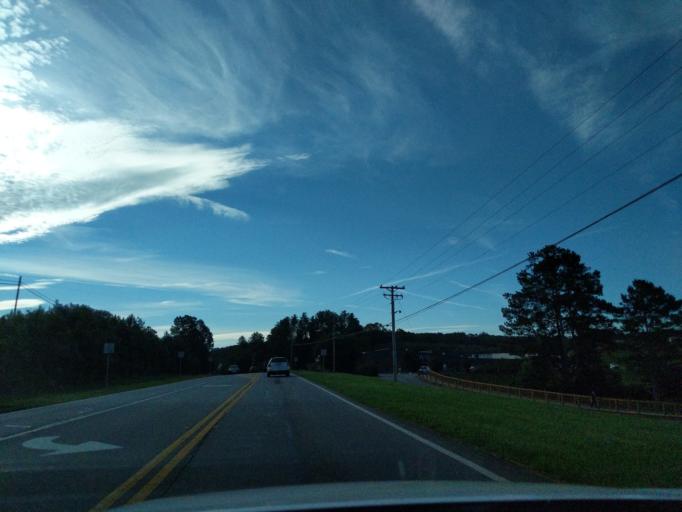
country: US
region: Georgia
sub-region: Fannin County
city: Blue Ridge
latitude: 34.8878
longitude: -84.3425
